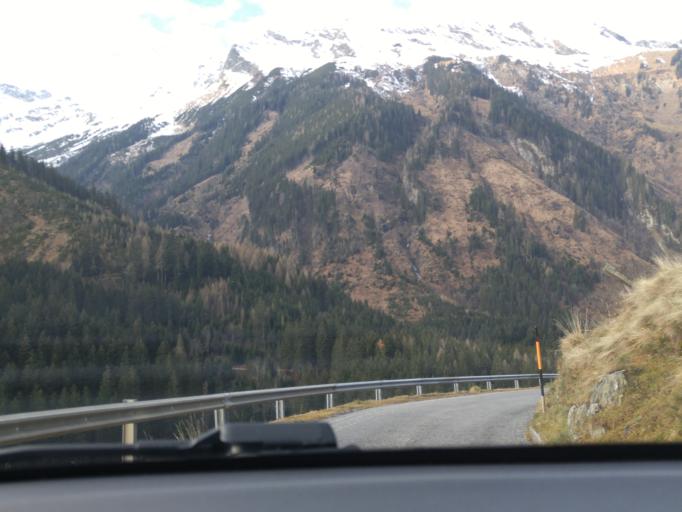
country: AT
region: Salzburg
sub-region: Politischer Bezirk Zell am See
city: Uttendorf
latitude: 47.1998
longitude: 12.6073
